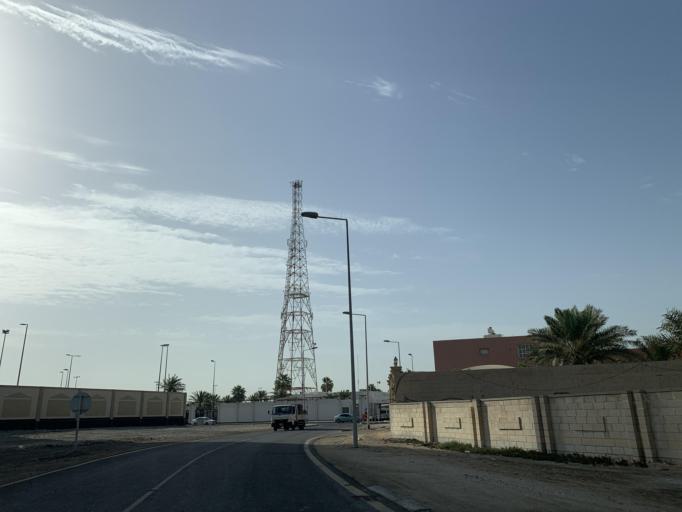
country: BH
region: Manama
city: Manama
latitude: 26.1841
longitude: 50.5883
